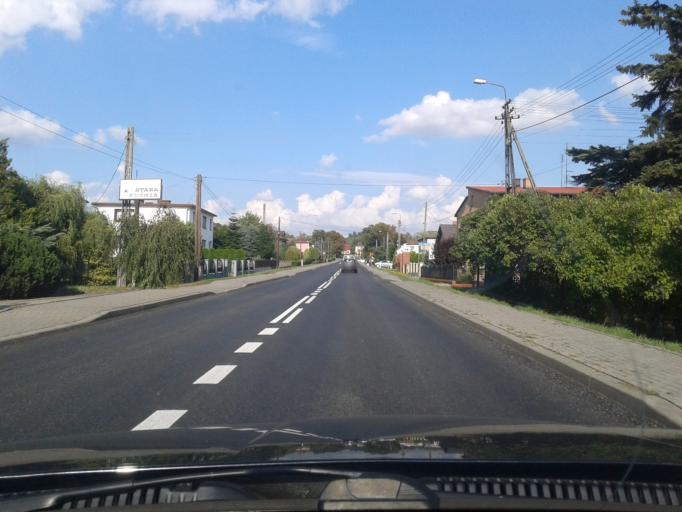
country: PL
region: Silesian Voivodeship
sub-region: Powiat wodzislawski
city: Gorzyce
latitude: 49.9580
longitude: 18.3849
